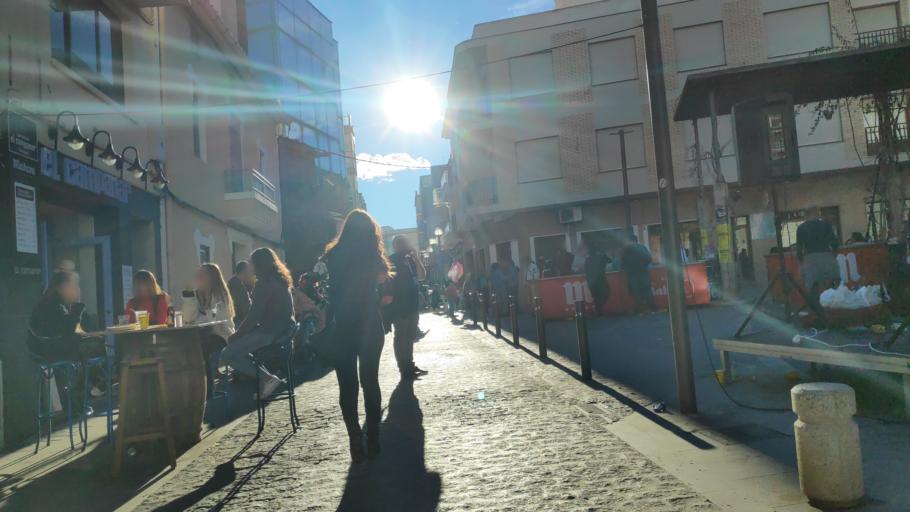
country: ES
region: Valencia
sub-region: Provincia de Castello
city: Benicassim
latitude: 40.0550
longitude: 0.0649
